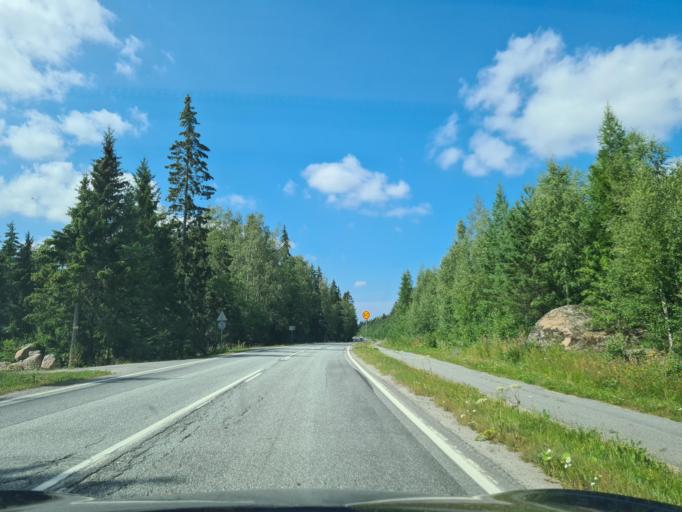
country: FI
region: Ostrobothnia
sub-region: Vaasa
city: Vaasa
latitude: 63.1957
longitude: 21.5468
